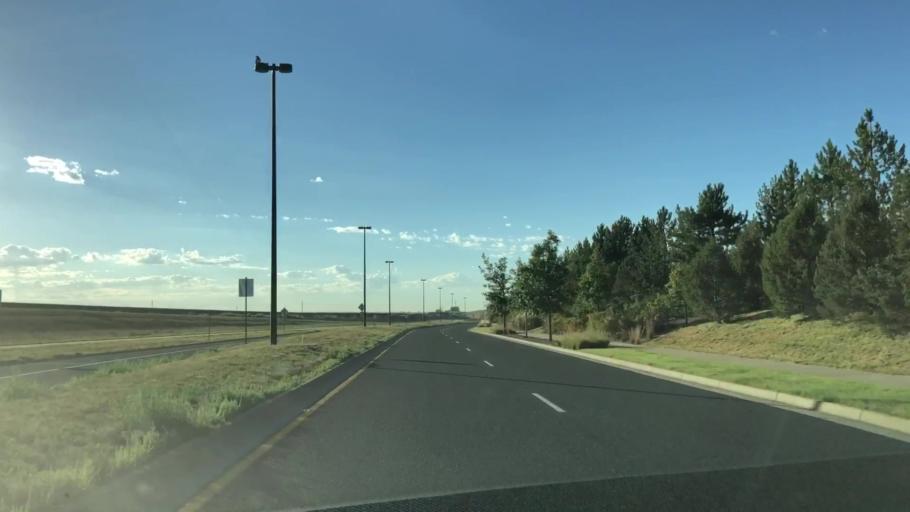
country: US
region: Colorado
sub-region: Larimer County
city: Loveland
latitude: 40.4208
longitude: -104.9903
